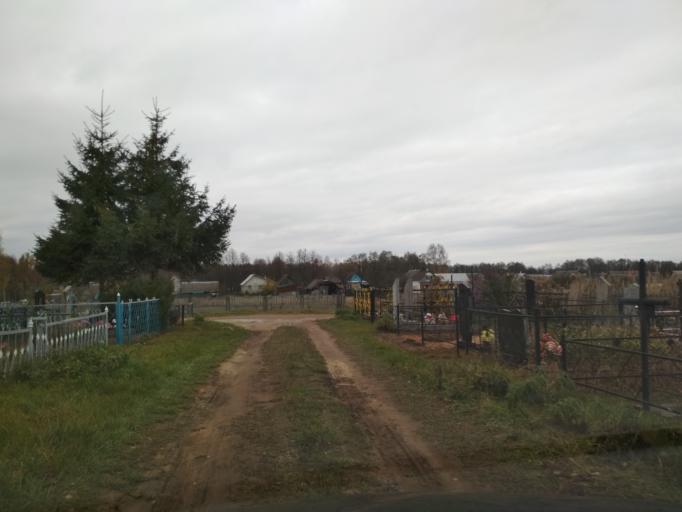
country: BY
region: Minsk
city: Blon'
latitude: 53.5207
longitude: 28.1803
